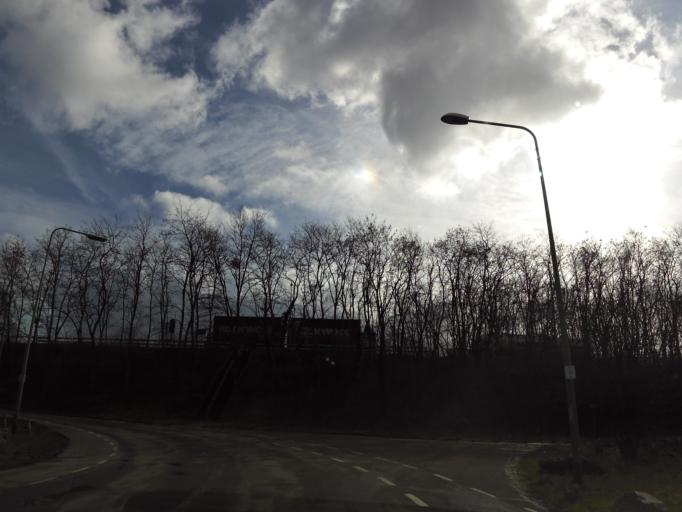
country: NL
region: Limburg
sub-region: Gemeente Meerssen
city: Meerssen
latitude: 50.8922
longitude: 5.7118
